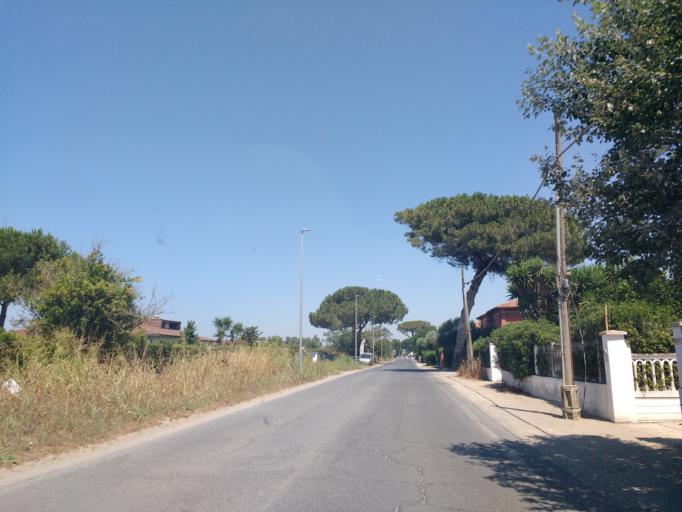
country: IT
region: Latium
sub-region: Citta metropolitana di Roma Capitale
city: Fregene
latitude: 41.8442
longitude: 12.2233
